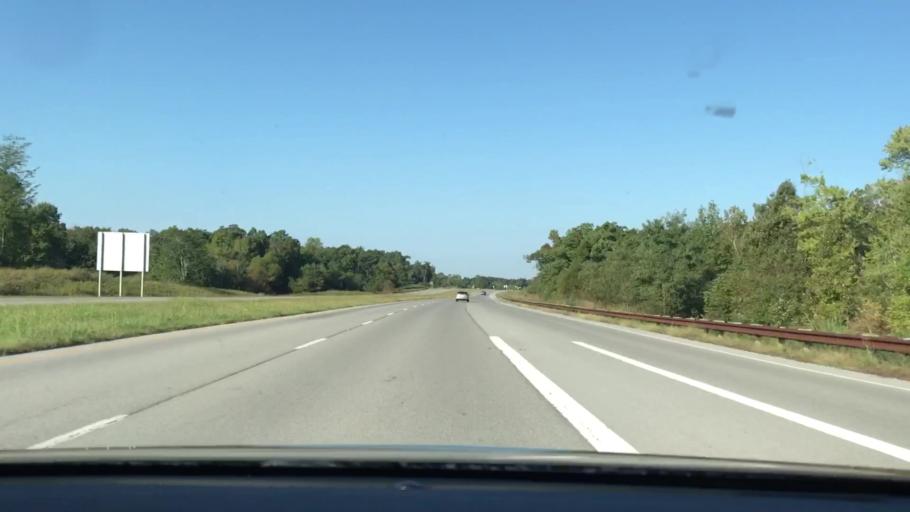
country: US
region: Kentucky
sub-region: Trigg County
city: Cadiz
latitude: 36.7791
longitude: -88.0697
